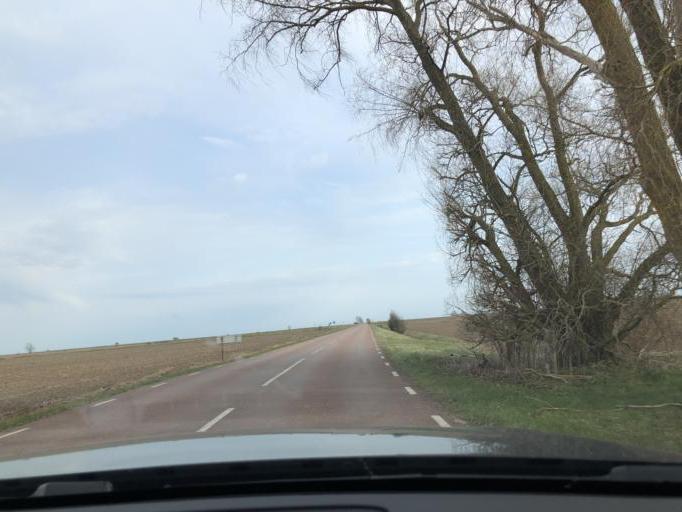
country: SE
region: Kalmar
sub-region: Morbylanga Kommun
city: Moerbylanga
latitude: 56.2866
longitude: 16.4896
